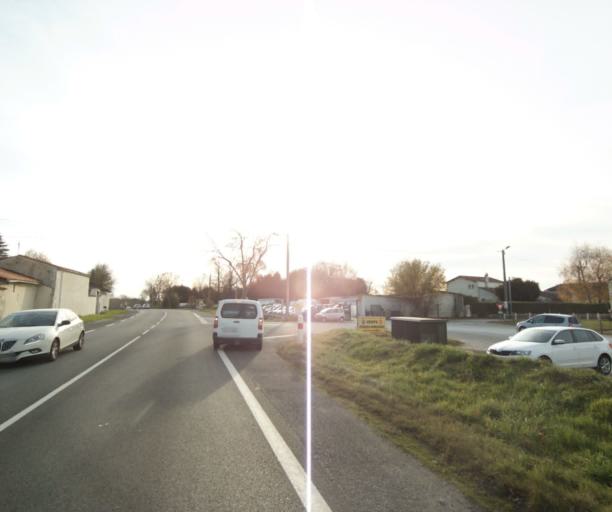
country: FR
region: Poitou-Charentes
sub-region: Departement de la Charente-Maritime
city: Fontcouverte
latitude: 45.7899
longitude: -0.5695
